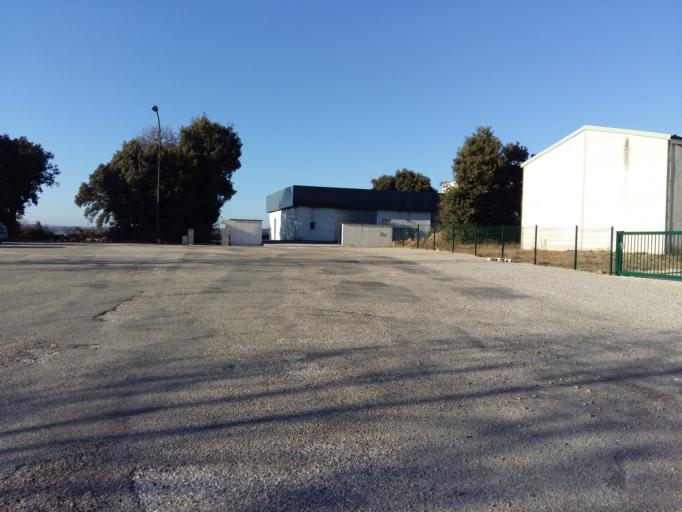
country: FR
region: Rhone-Alpes
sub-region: Departement de la Drome
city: Grignan
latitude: 44.4233
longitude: 4.8916
